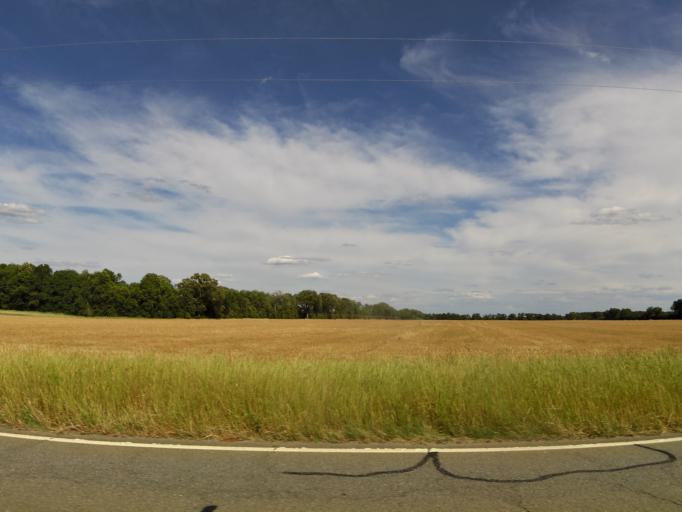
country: US
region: South Carolina
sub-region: Bamberg County
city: Denmark
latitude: 33.1980
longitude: -81.1787
